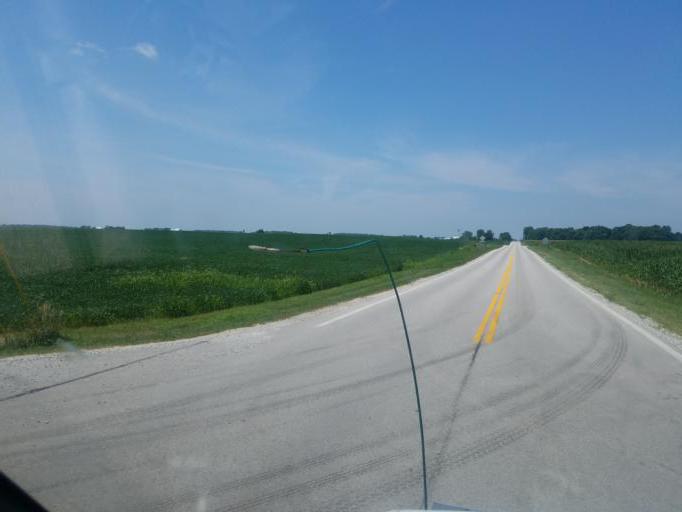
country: US
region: Ohio
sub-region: Auglaize County
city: New Bremen
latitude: 40.4222
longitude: -84.4337
